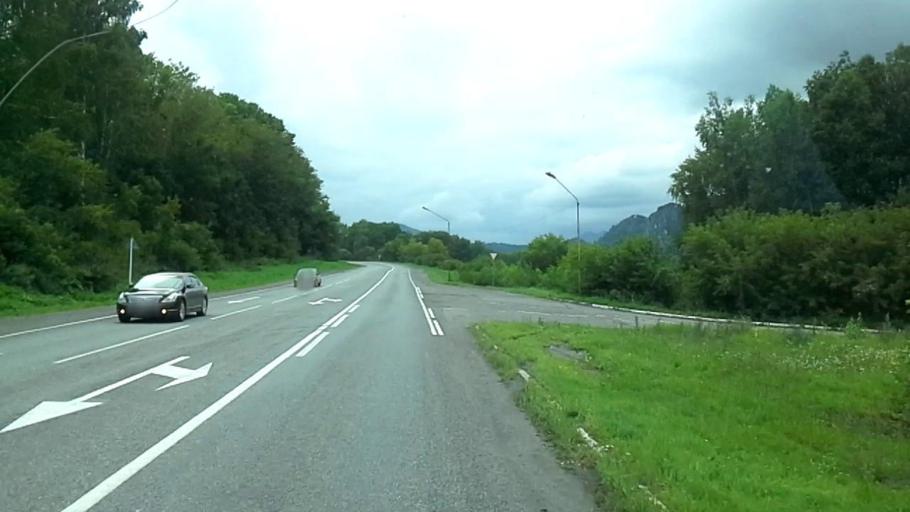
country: RU
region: Altay
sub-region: Mayminskiy Rayon
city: Manzherok
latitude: 51.8640
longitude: 85.7640
